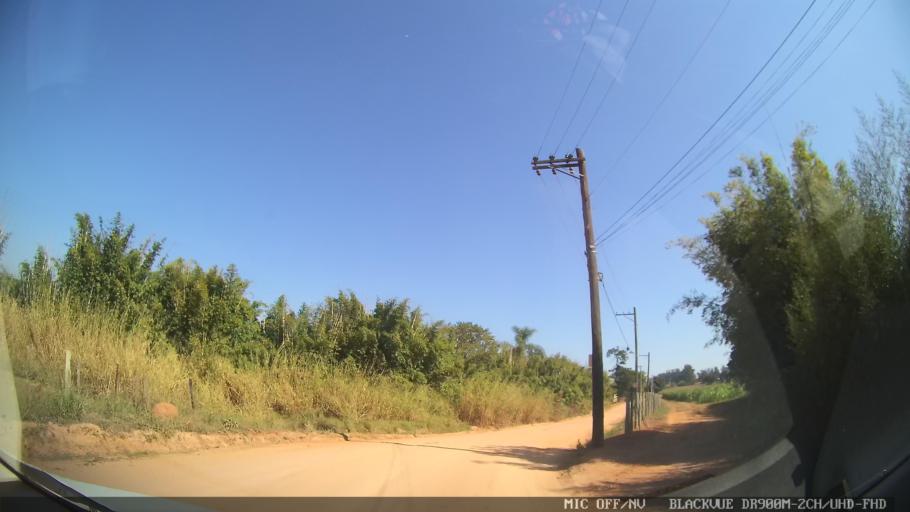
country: BR
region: Sao Paulo
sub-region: Itupeva
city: Itupeva
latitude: -23.1259
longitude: -47.0790
